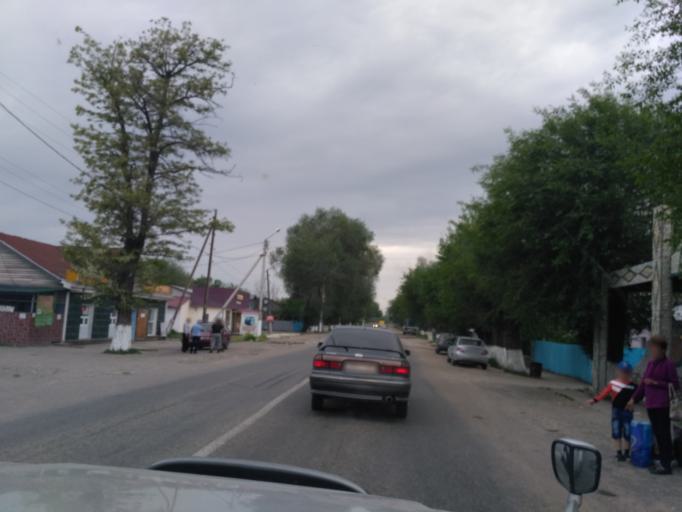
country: KZ
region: Almaty Oblysy
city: Burunday
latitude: 43.4602
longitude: 76.7255
